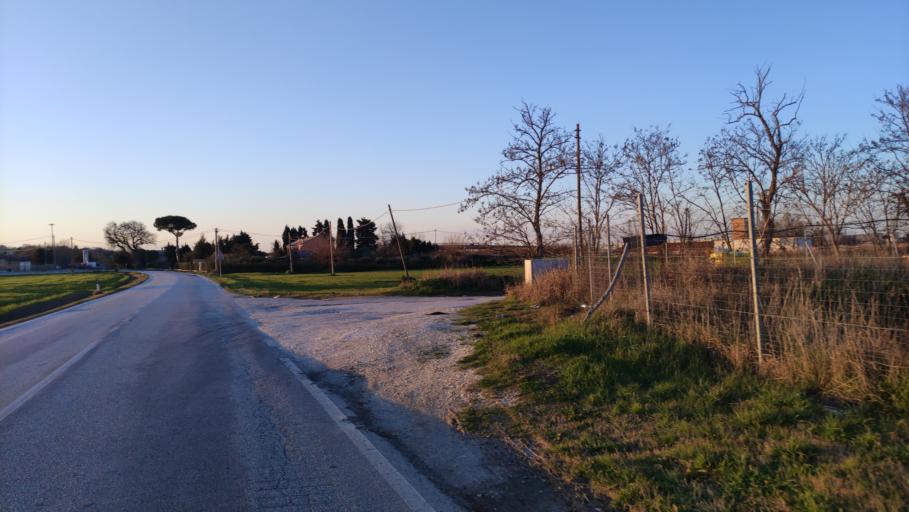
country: IT
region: The Marches
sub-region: Provincia di Pesaro e Urbino
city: Marotta
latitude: 43.7532
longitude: 13.1440
